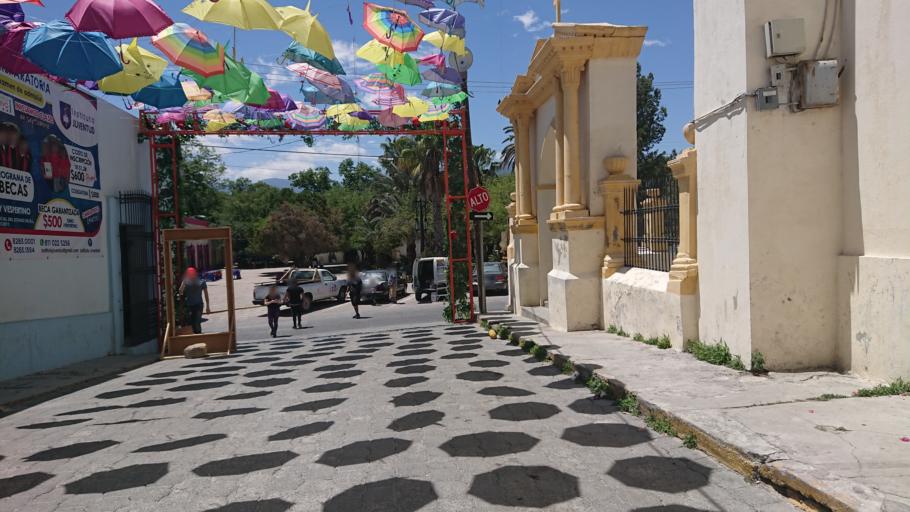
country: MX
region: Nuevo Leon
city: Garcia
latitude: 25.8121
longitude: -100.5945
